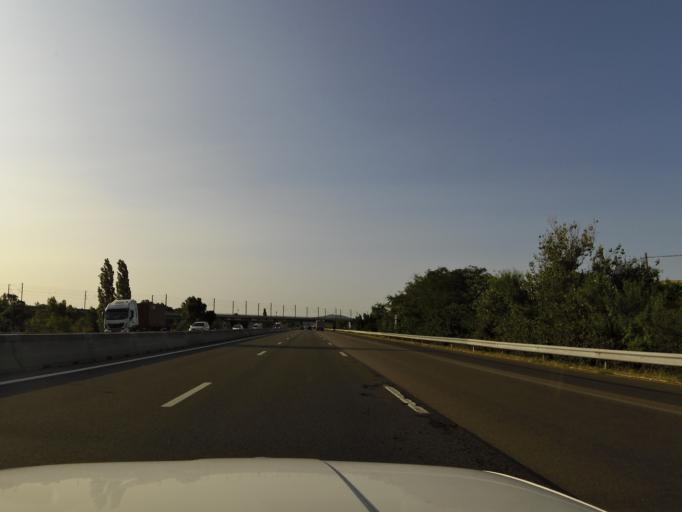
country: FR
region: Rhone-Alpes
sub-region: Departement de la Drome
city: Pierrelatte
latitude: 44.3744
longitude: 4.7329
